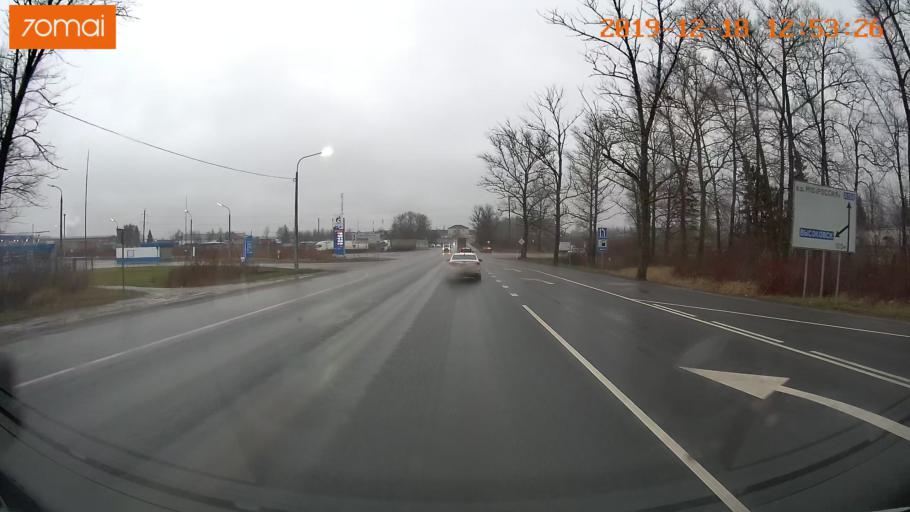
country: RU
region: Moskovskaya
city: Klin
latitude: 56.3190
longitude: 36.6942
